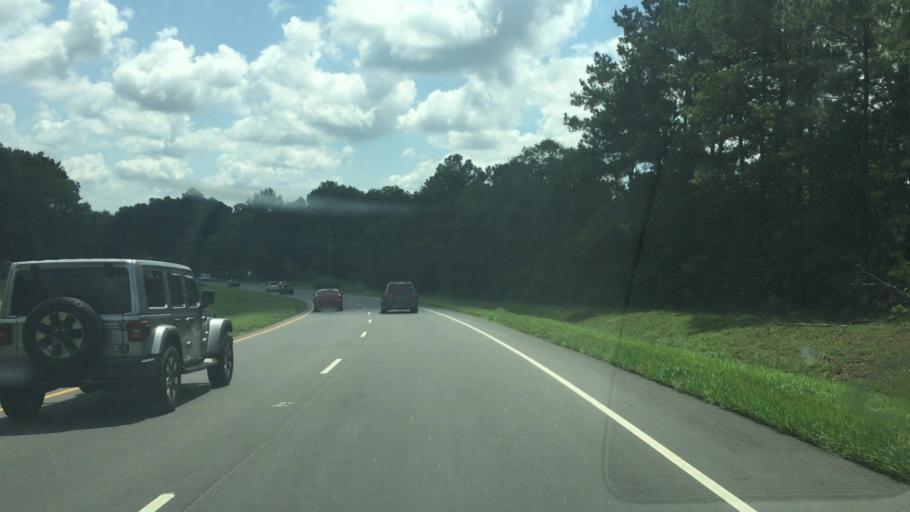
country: US
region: North Carolina
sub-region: Scotland County
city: Laurel Hill
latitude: 34.8003
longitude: -79.5353
